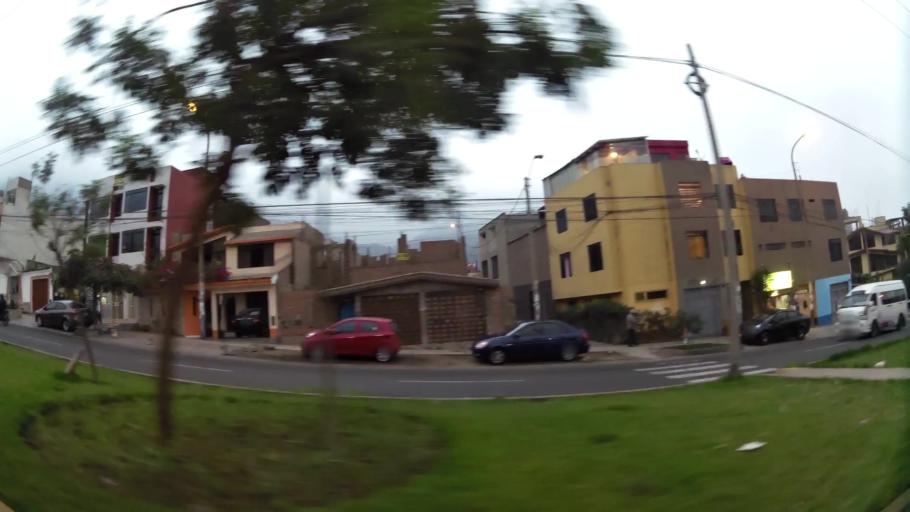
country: PE
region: Lima
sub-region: Lima
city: La Molina
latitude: -12.1123
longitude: -76.9373
